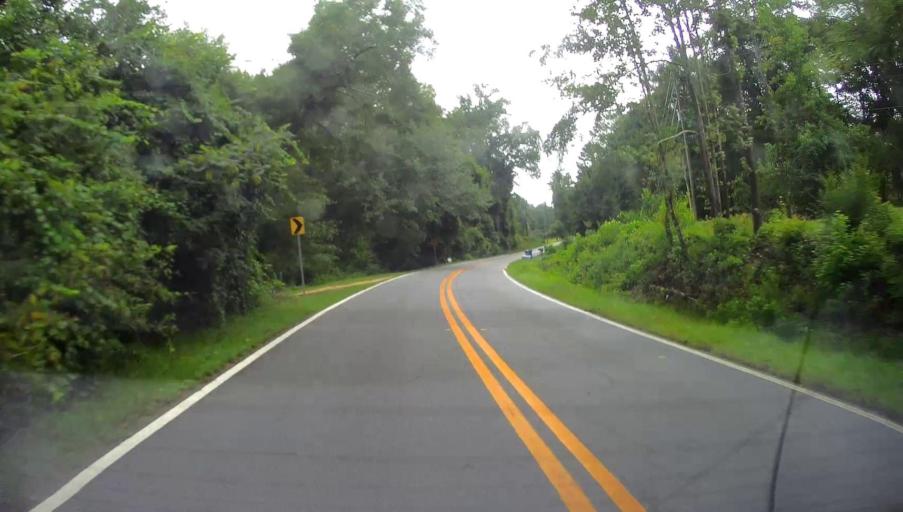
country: US
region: Georgia
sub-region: Bibb County
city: West Point
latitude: 32.7858
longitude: -83.7700
